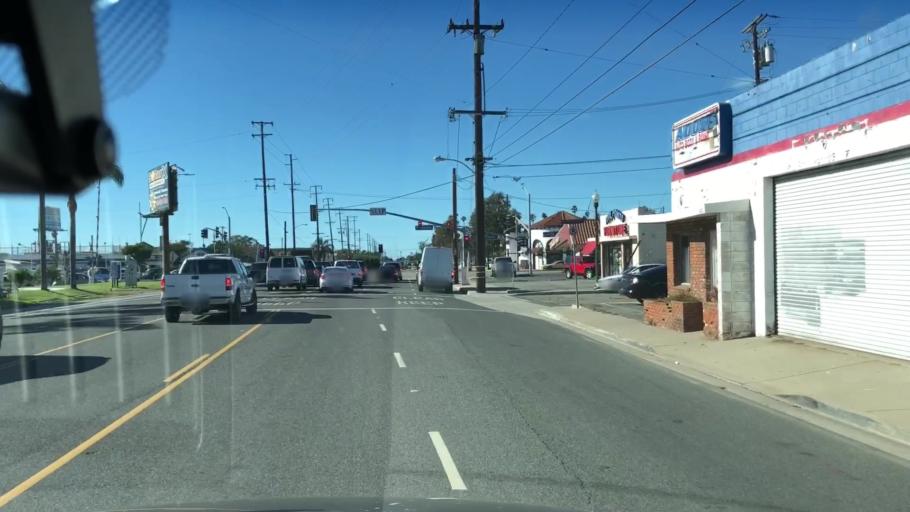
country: US
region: California
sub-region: Ventura County
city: Oxnard
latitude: 34.1901
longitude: -119.1762
